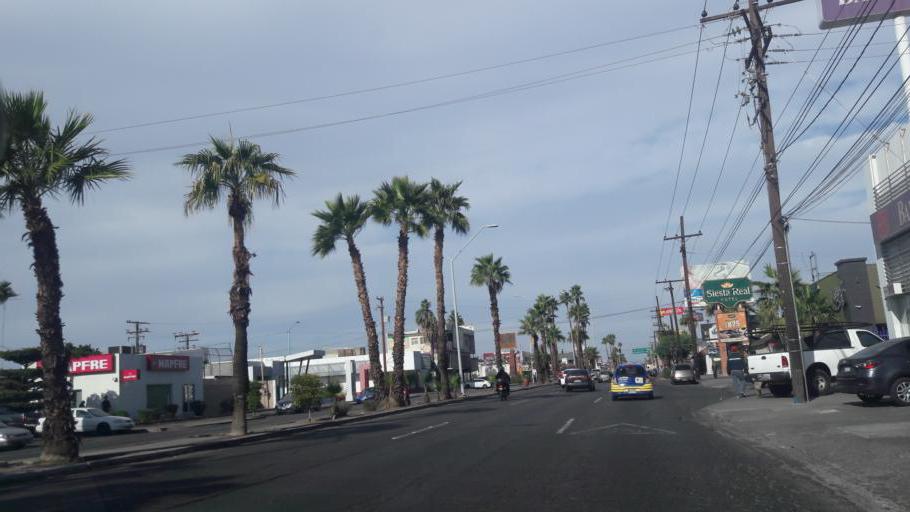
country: MX
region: Baja California
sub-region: Mexicali
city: Mexicali
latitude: 32.6555
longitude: -115.4524
